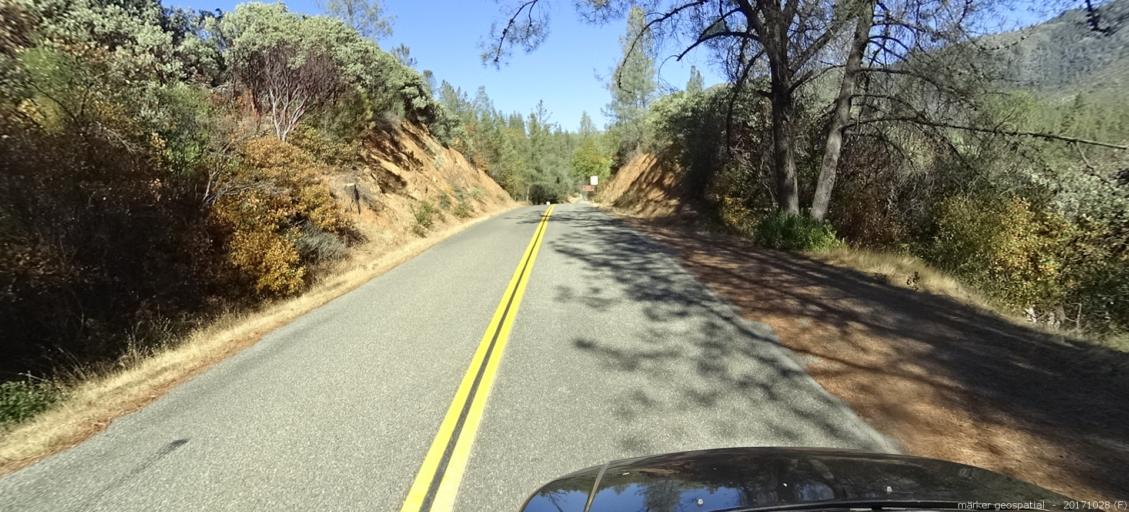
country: US
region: California
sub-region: Shasta County
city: Shasta
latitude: 40.6462
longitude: -122.5577
